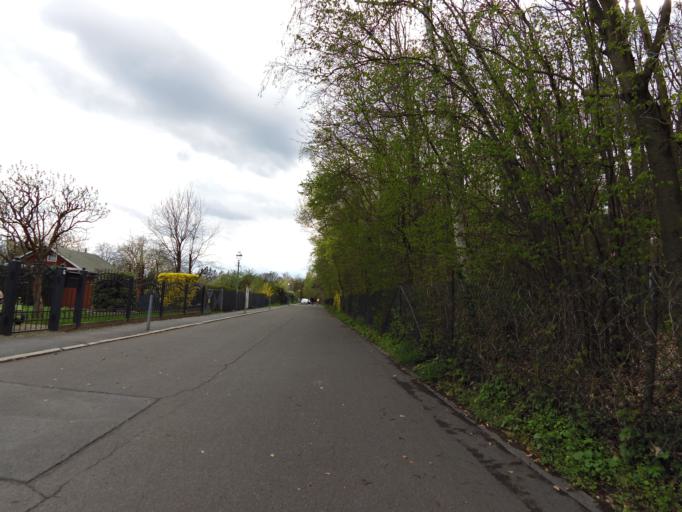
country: DE
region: Berlin
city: Lichtenrade
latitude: 52.4001
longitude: 13.3899
